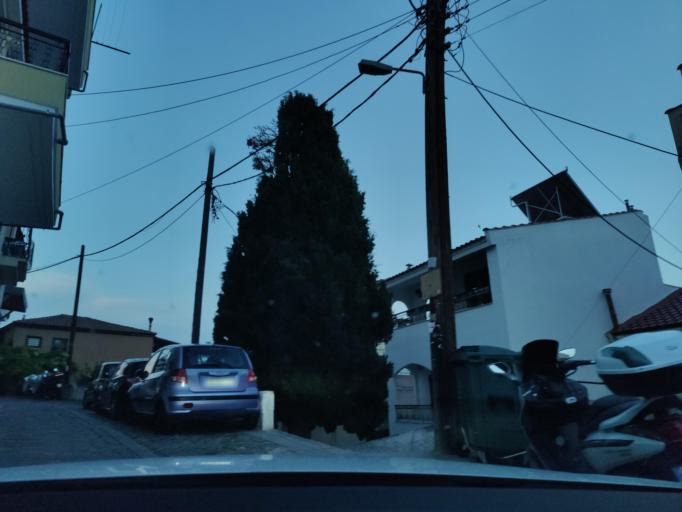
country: GR
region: East Macedonia and Thrace
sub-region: Nomos Kavalas
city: Kavala
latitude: 40.9343
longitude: 24.4174
